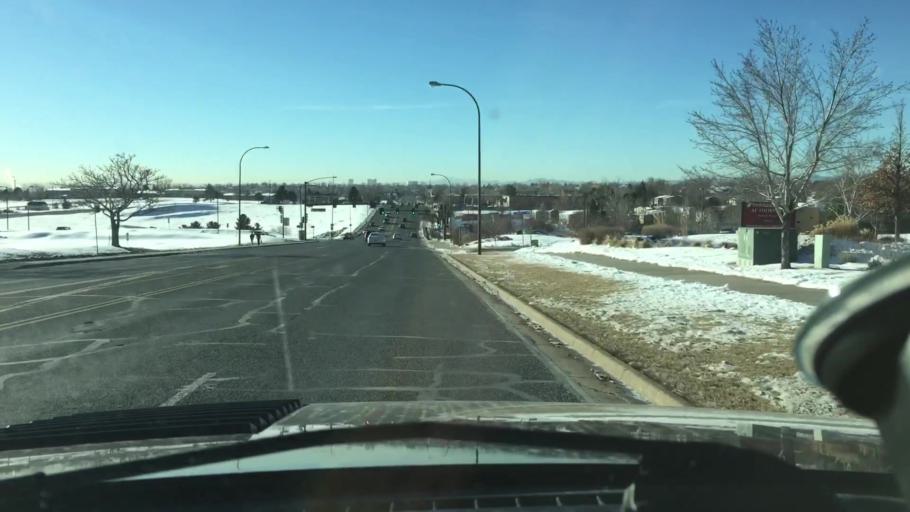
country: US
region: Colorado
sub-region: Adams County
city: Federal Heights
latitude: 39.8681
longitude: -104.9967
